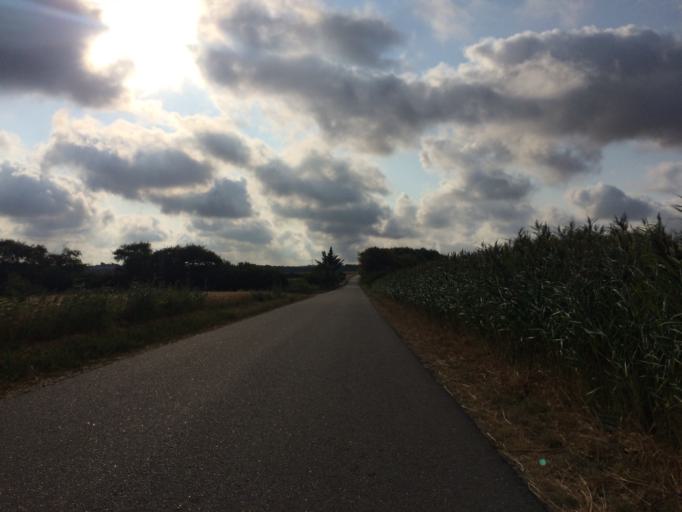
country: DK
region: Central Jutland
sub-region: Holstebro Kommune
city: Vinderup
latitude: 56.6133
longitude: 8.7673
